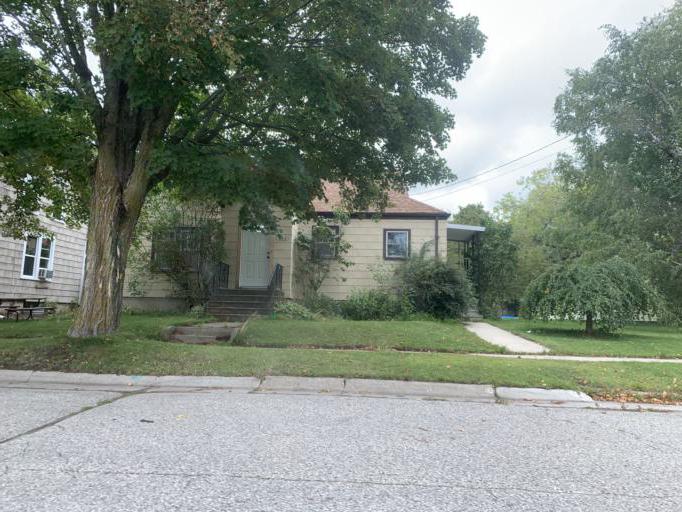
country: US
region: Wisconsin
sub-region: Door County
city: Sturgeon Bay
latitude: 44.8405
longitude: -87.3754
